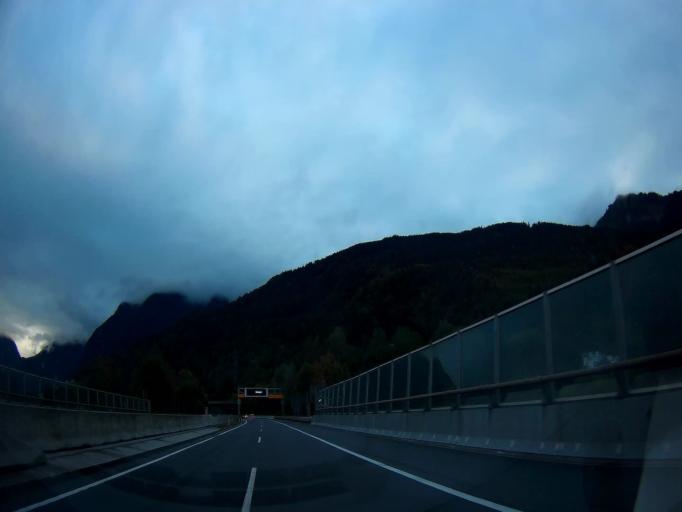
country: AT
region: Salzburg
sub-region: Politischer Bezirk Hallein
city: Kuchl
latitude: 47.6343
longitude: 13.1326
